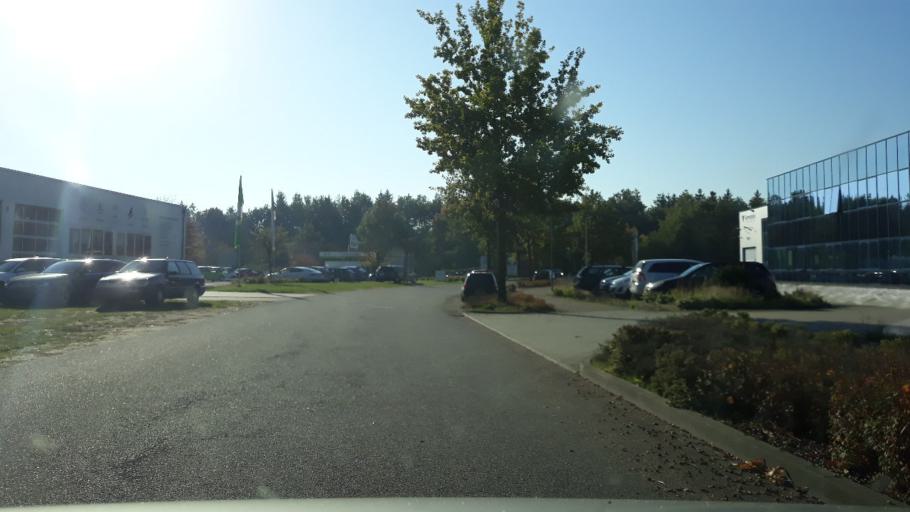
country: DE
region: Schleswig-Holstein
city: Kropp
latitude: 54.4136
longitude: 9.5285
